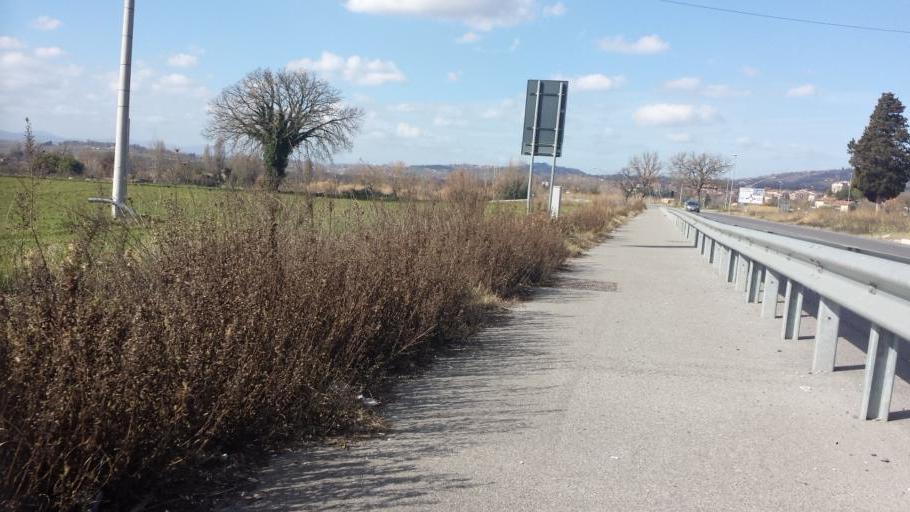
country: IT
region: Umbria
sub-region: Provincia di Terni
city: Terni
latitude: 42.5766
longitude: 12.5970
